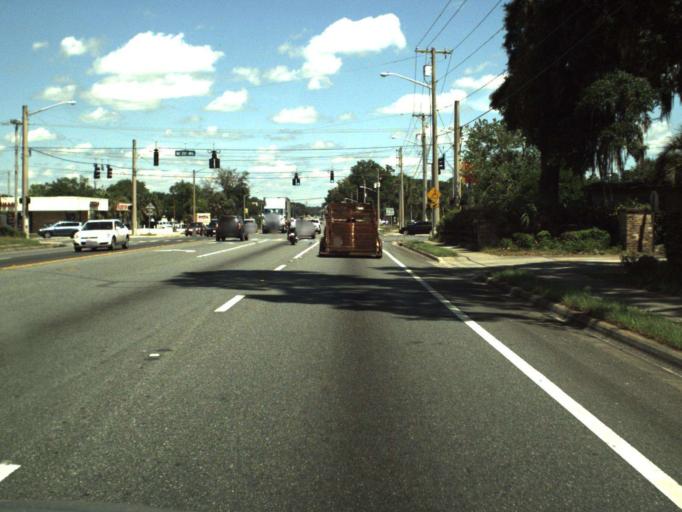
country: US
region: Florida
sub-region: Marion County
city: Ocala
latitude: 29.2005
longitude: -82.1042
